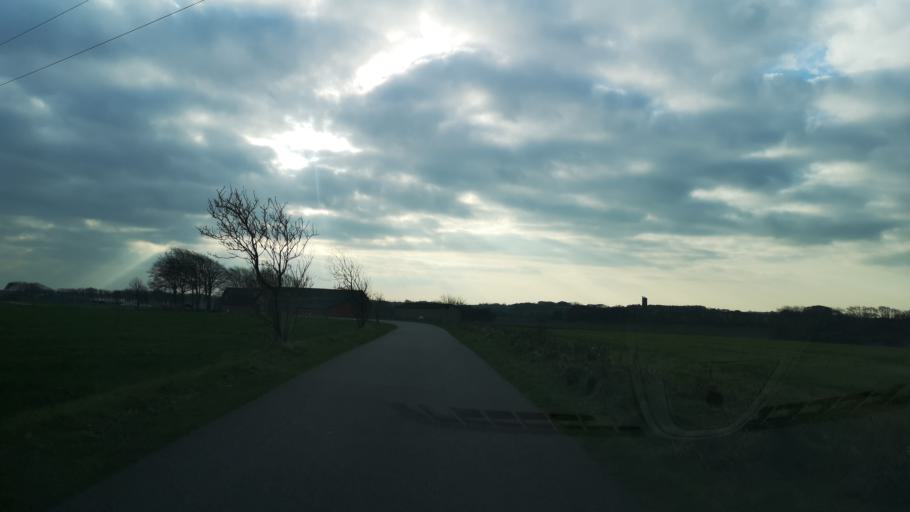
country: DK
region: Central Jutland
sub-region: Ringkobing-Skjern Kommune
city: Videbaek
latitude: 56.0001
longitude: 8.5880
